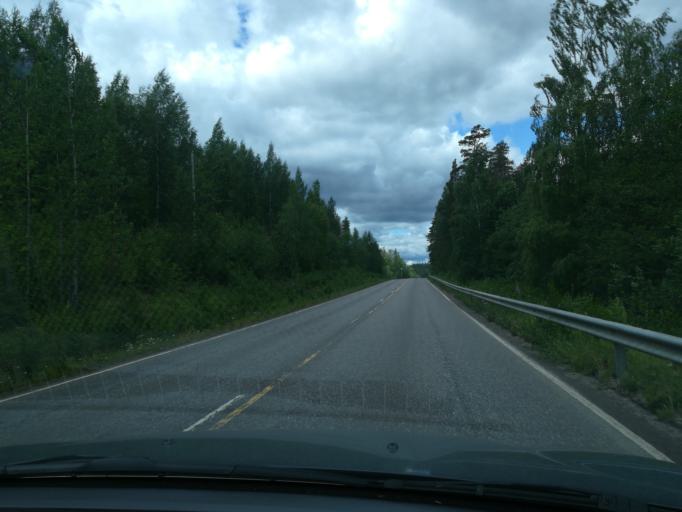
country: FI
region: Southern Savonia
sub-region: Mikkeli
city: Maentyharju
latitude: 61.3646
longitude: 26.9738
